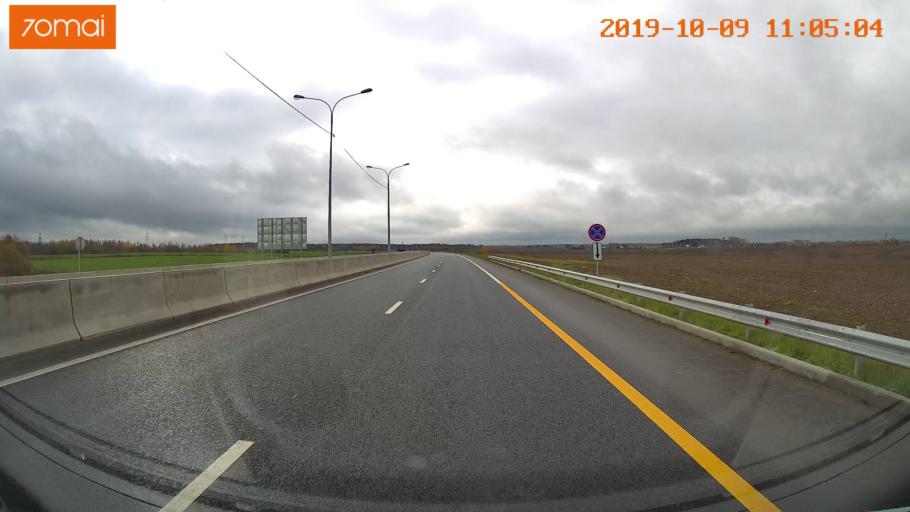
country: RU
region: Vologda
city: Molochnoye
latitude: 59.2045
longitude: 39.7603
